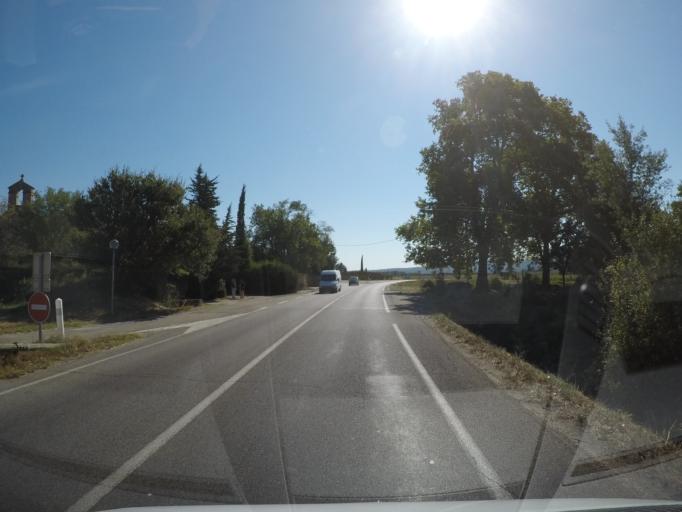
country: FR
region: Languedoc-Roussillon
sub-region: Departement du Gard
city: Castillon-du-Gard
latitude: 43.9726
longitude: 4.4968
